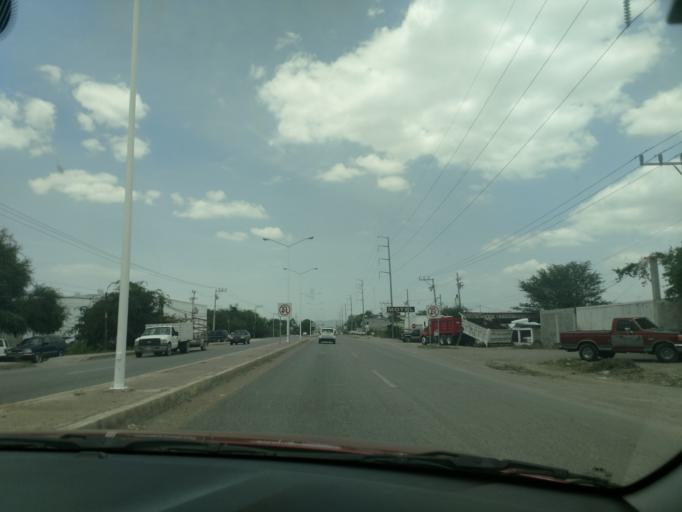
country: MX
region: San Luis Potosi
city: Rio Verde
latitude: 21.9220
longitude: -99.9732
